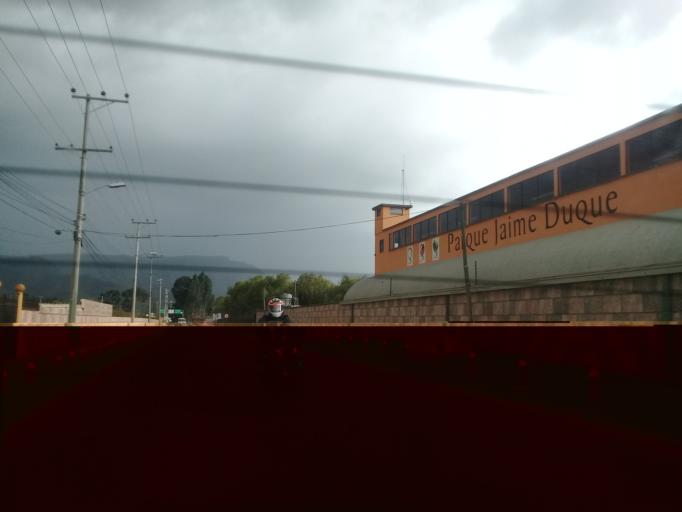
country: CO
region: Cundinamarca
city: Sopo
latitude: 4.9466
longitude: -73.9606
